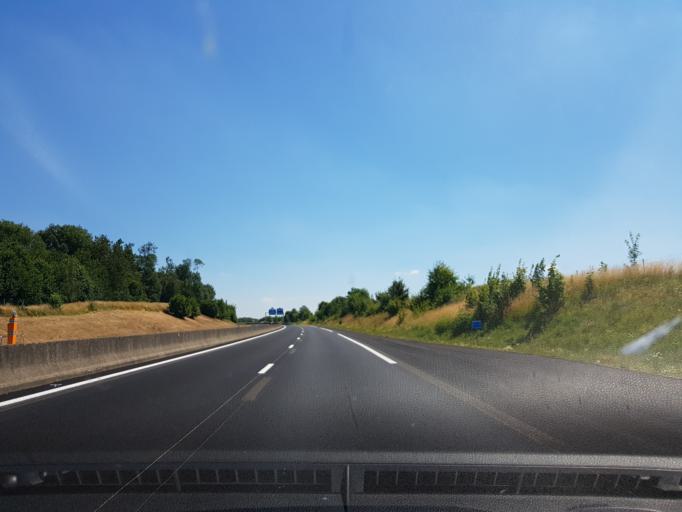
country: FR
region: Picardie
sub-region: Departement de l'Aisne
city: Holnon
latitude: 49.8430
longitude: 3.2101
